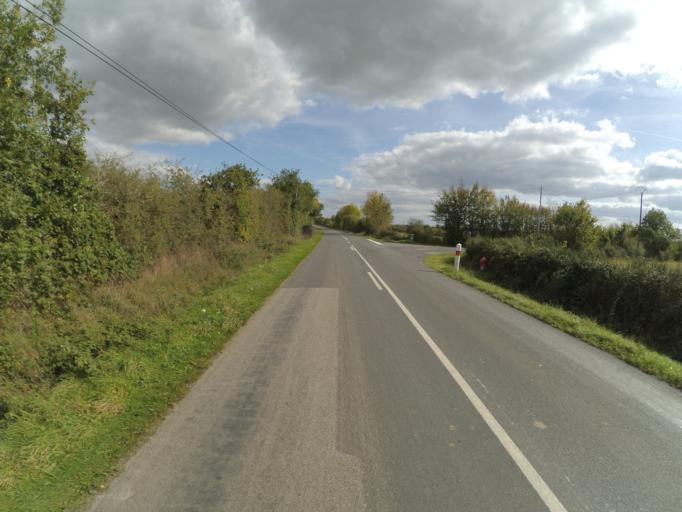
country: FR
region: Pays de la Loire
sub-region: Departement de la Loire-Atlantique
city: Casson
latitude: 47.4012
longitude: -1.5796
